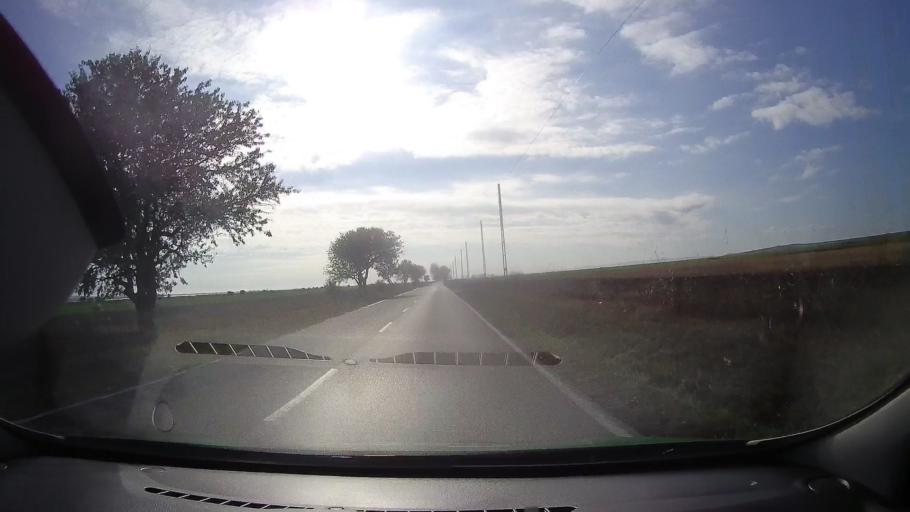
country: RO
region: Tulcea
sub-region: Comuna Valea Nucarilor
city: Agighiol
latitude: 45.0182
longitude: 28.8831
